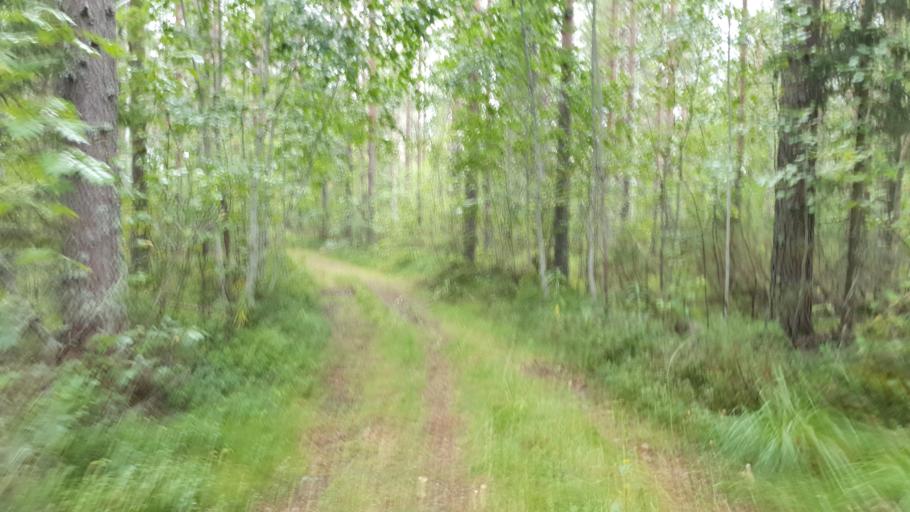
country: FI
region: Kainuu
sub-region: Kehys-Kainuu
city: Kuhmo
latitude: 64.1463
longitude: 29.3407
